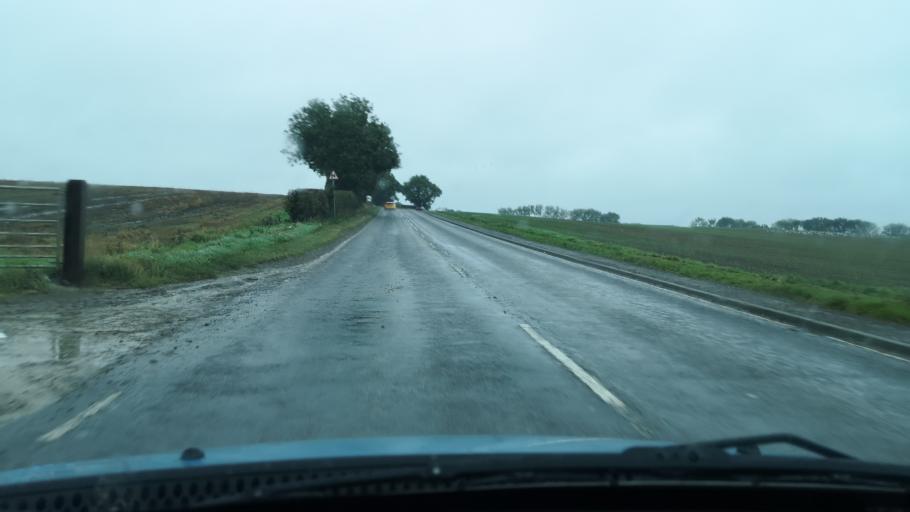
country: GB
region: England
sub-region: City and Borough of Wakefield
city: Low Ackworth
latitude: 53.6337
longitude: -1.3356
